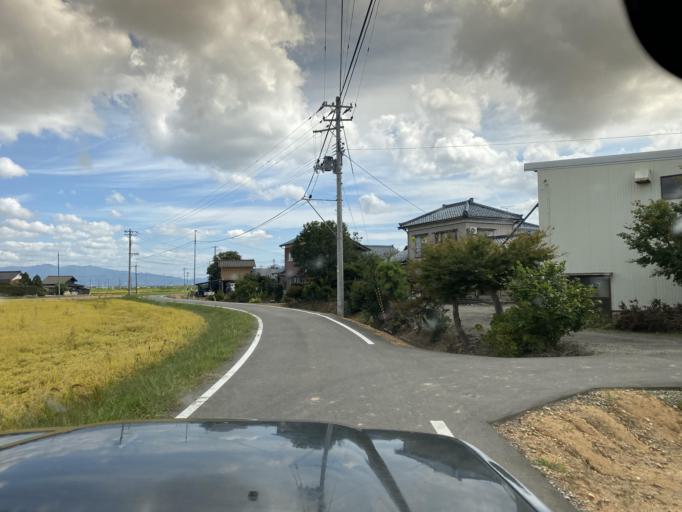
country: JP
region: Niigata
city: Niitsu-honcho
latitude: 37.8176
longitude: 139.0786
